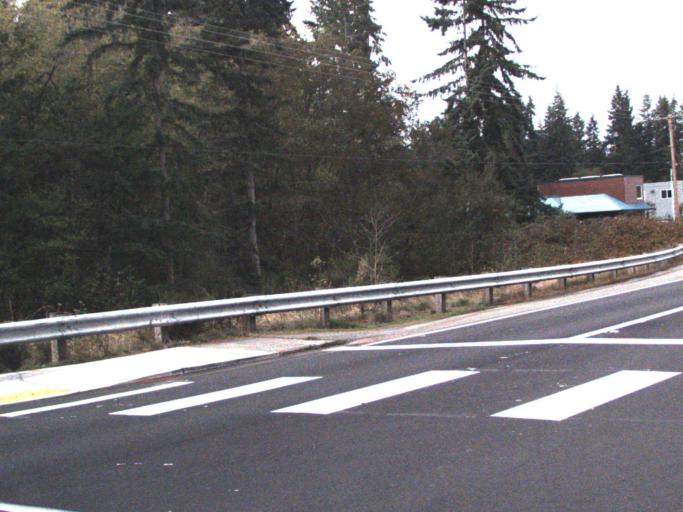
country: US
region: Washington
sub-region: Island County
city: Langley
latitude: 47.9913
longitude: -122.3966
